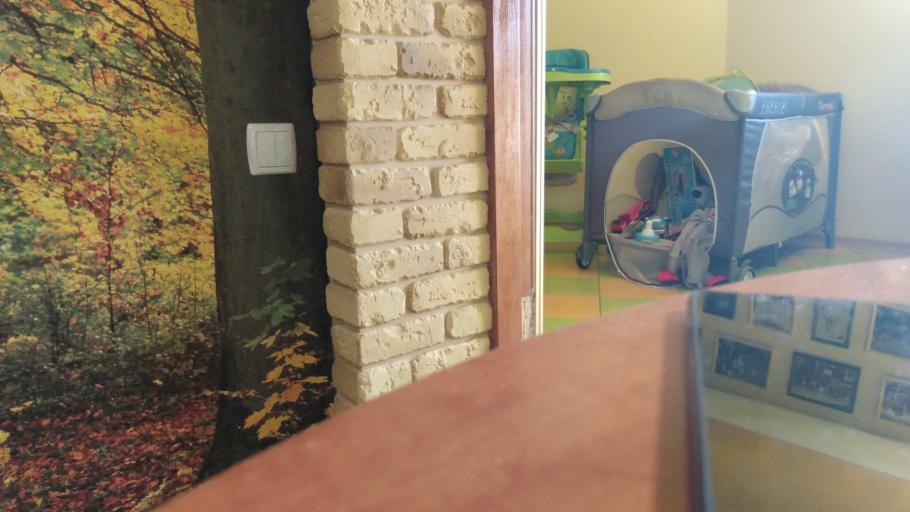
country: RU
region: Tverskaya
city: Bologoye
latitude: 57.9079
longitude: 34.2417
